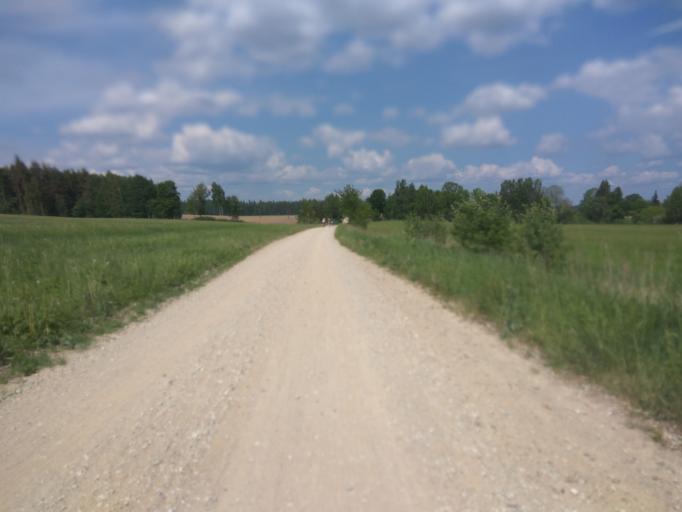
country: LV
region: Kuldigas Rajons
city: Kuldiga
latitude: 56.9070
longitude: 21.9490
